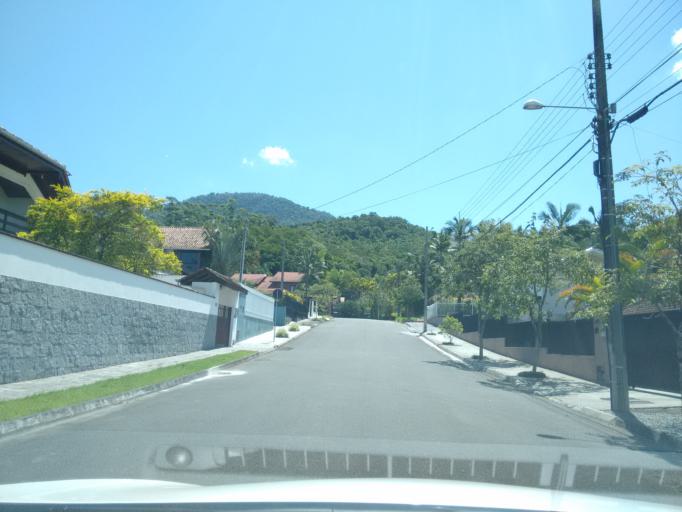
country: BR
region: Santa Catarina
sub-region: Pomerode
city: Pomerode
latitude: -26.7558
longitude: -49.1801
